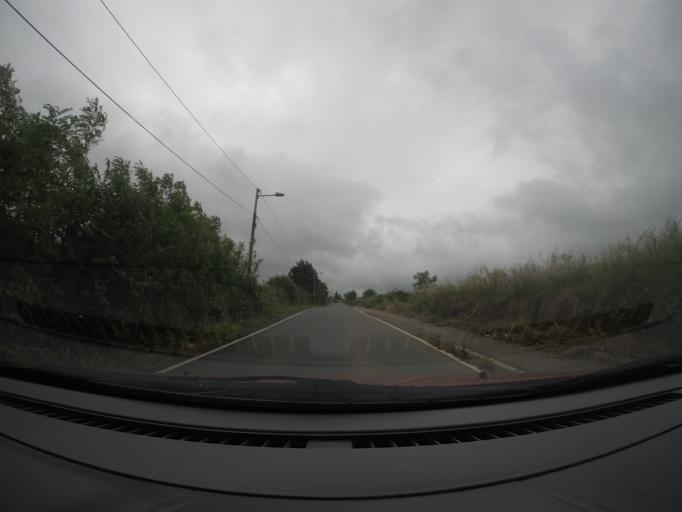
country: RS
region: Central Serbia
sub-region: Belgrade
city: Zvezdara
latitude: 44.7025
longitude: 20.5632
